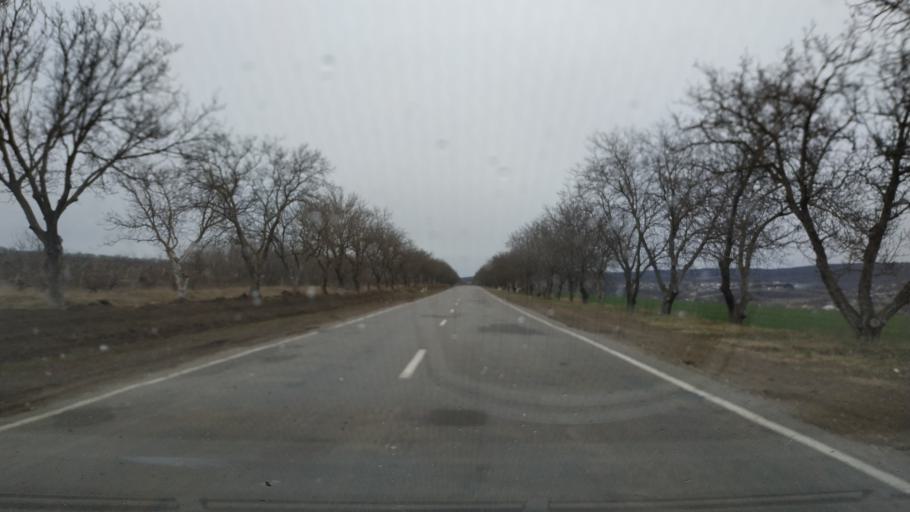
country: MD
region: Hincesti
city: Hincesti
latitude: 46.7829
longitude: 28.5245
